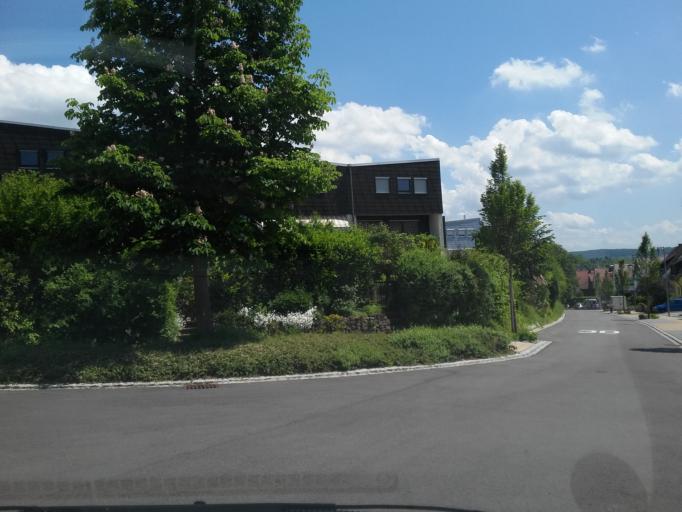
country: DE
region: Baden-Wuerttemberg
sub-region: Regierungsbezirk Stuttgart
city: Untergruppenbach
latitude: 49.0932
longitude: 9.2706
